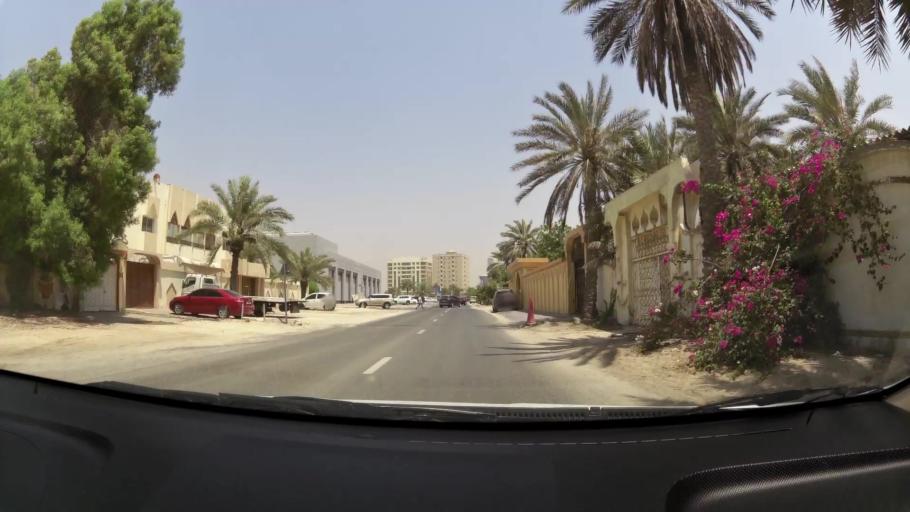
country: AE
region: Ajman
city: Ajman
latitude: 25.4003
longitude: 55.4322
